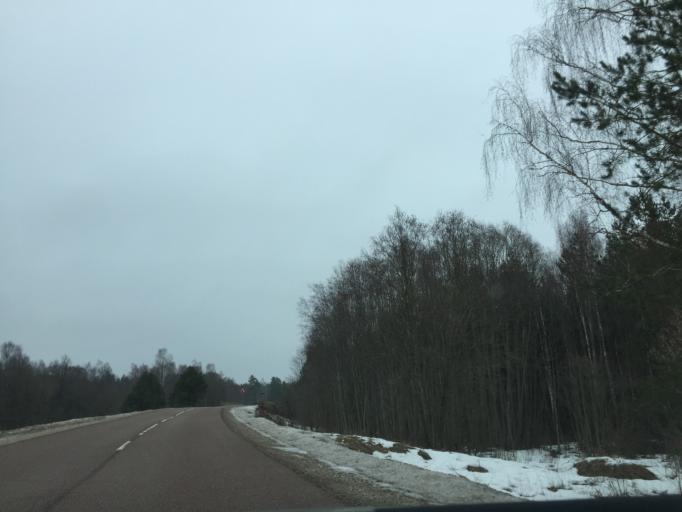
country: LV
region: Olaine
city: Olaine
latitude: 56.6393
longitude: 23.9374
